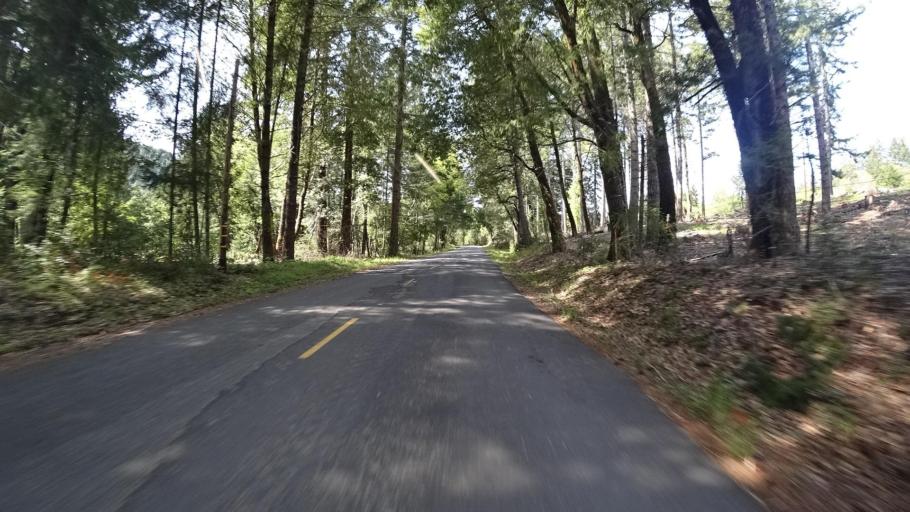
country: US
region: California
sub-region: Humboldt County
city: Redway
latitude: 40.3758
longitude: -123.7410
